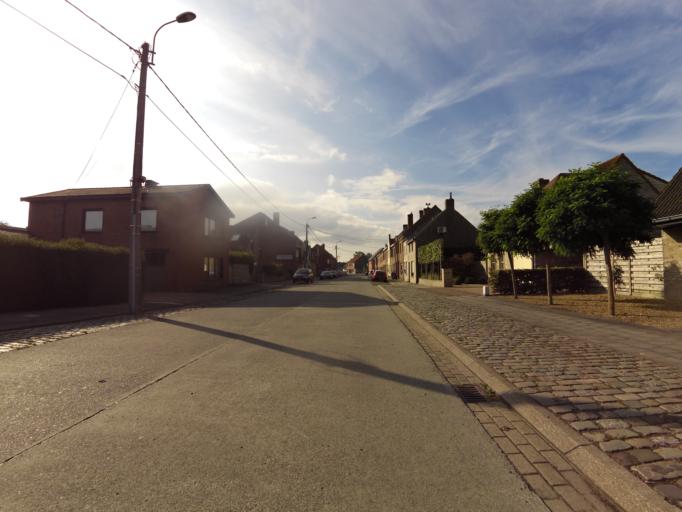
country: BE
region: Flanders
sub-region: Provincie West-Vlaanderen
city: Gistel
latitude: 51.1771
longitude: 2.9347
